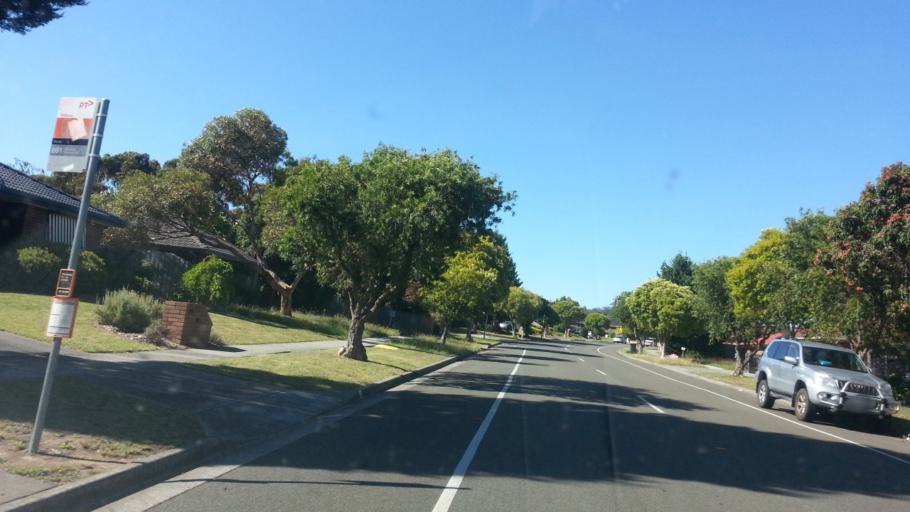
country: AU
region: Victoria
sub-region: Yarra Ranges
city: Lysterfield
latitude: -37.9216
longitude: 145.2687
